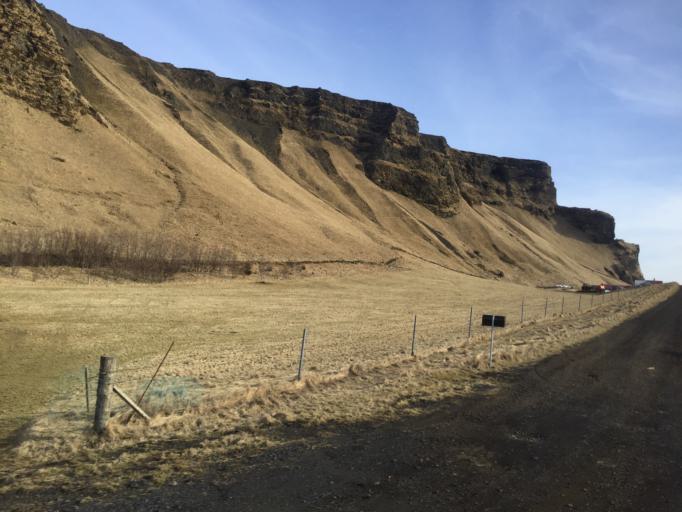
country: IS
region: South
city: Vestmannaeyjar
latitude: 63.4074
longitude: -19.0480
